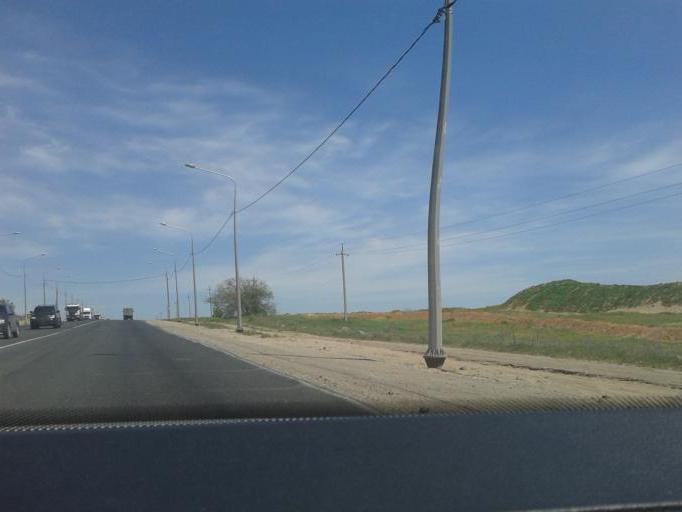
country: RU
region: Volgograd
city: Vodstroy
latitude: 48.8119
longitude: 44.5240
